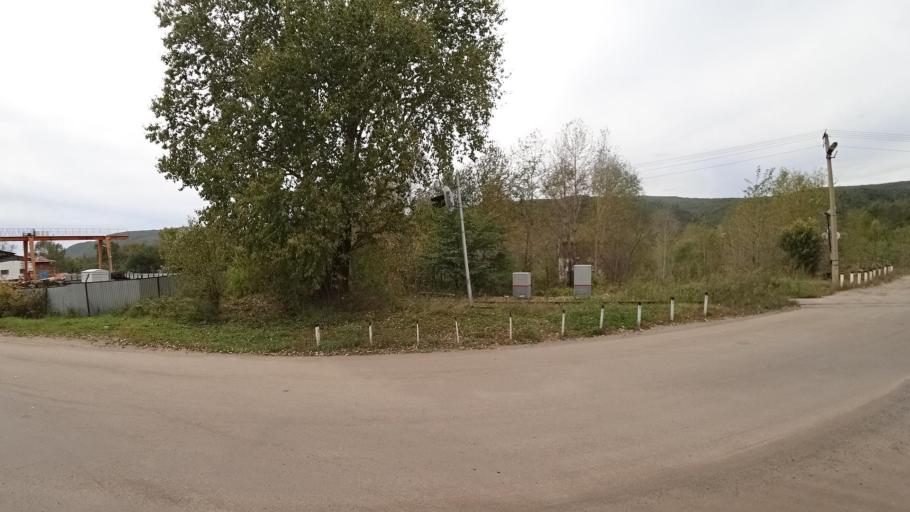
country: RU
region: Jewish Autonomous Oblast
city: Khingansk
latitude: 49.0208
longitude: 131.0548
